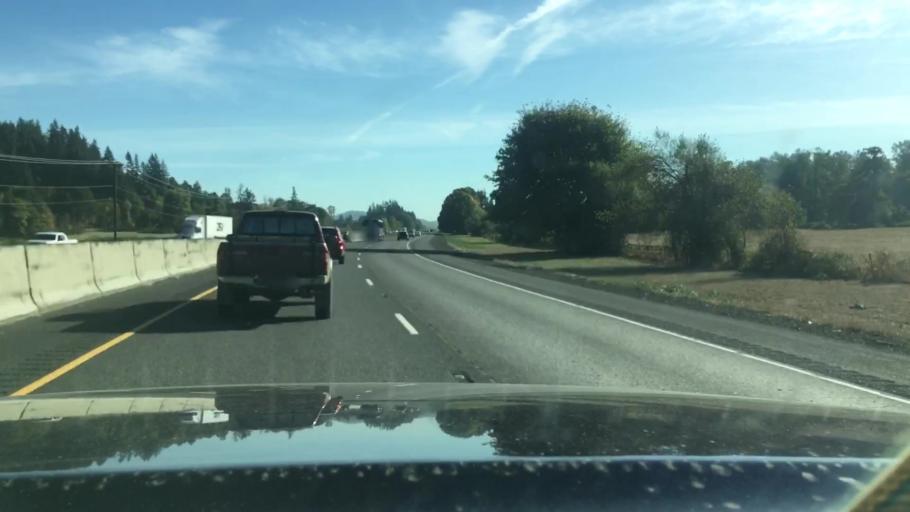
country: US
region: Oregon
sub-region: Lane County
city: Creswell
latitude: 43.8682
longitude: -123.0141
